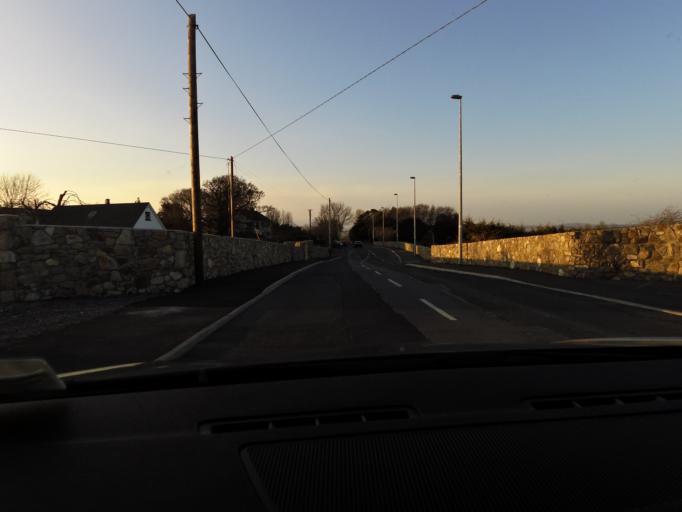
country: IE
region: Connaught
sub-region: County Galway
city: Gaillimh
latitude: 53.2862
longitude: -9.0820
